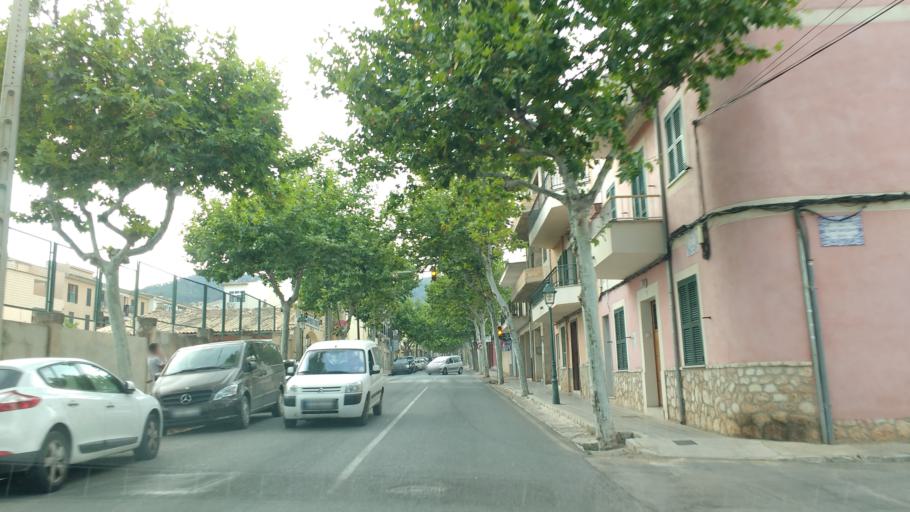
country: ES
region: Balearic Islands
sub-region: Illes Balears
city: Alaro
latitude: 39.7025
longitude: 2.7942
